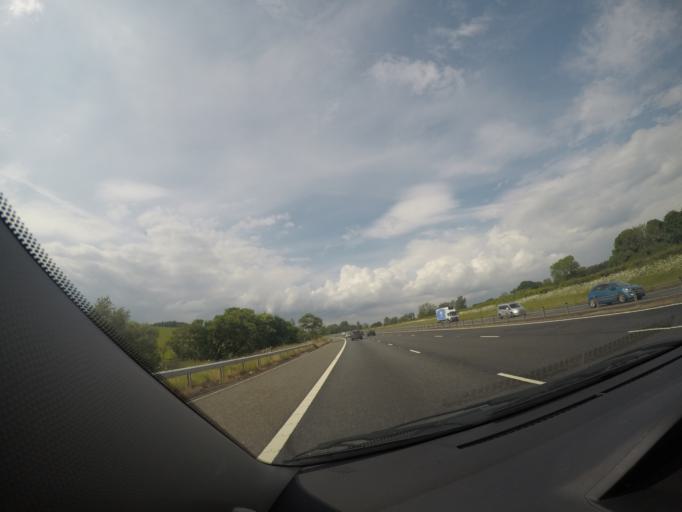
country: GB
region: Scotland
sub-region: Dumfries and Galloway
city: Lockerbie
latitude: 55.1631
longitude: -3.3873
